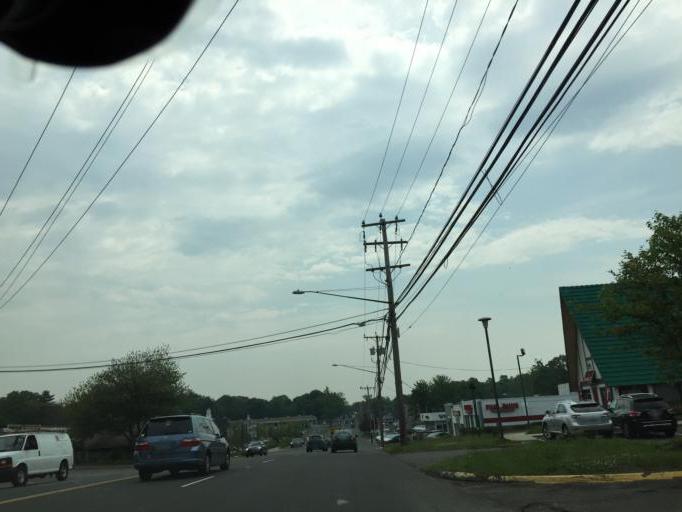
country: US
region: Connecticut
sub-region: Fairfield County
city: Westport
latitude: 41.1396
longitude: -73.3477
